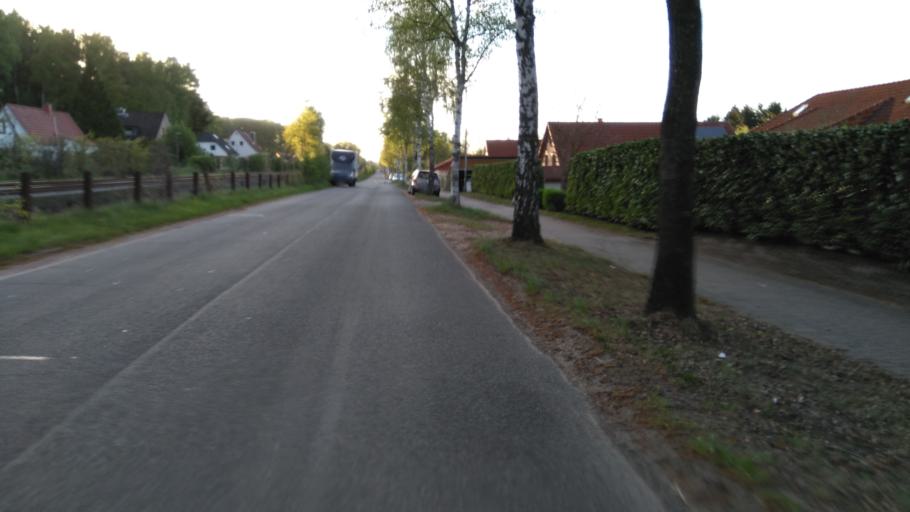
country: DE
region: Lower Saxony
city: Buxtehude
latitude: 53.4765
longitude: 9.6520
